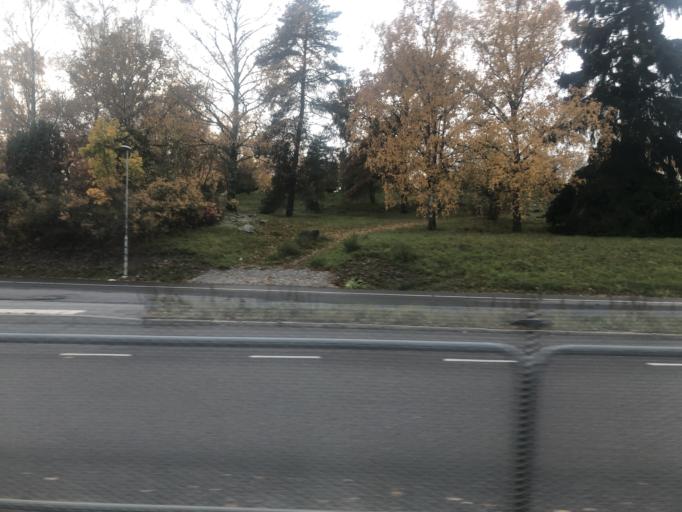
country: SE
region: Stockholm
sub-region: Jarfalla Kommun
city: Jakobsberg
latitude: 59.4190
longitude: 17.8301
